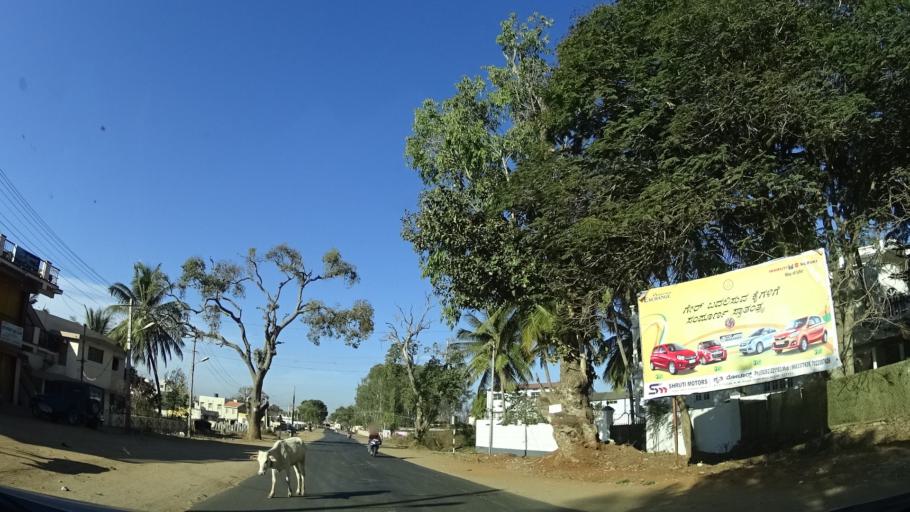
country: IN
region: Karnataka
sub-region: Chikmagalur
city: Chikmagalur
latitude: 13.3306
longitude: 75.7888
